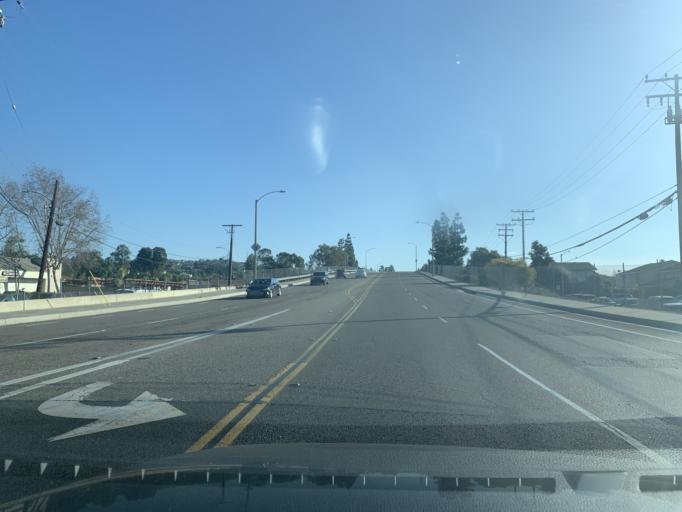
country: US
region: California
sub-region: Orange County
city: Villa Park
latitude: 33.8230
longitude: -117.8347
